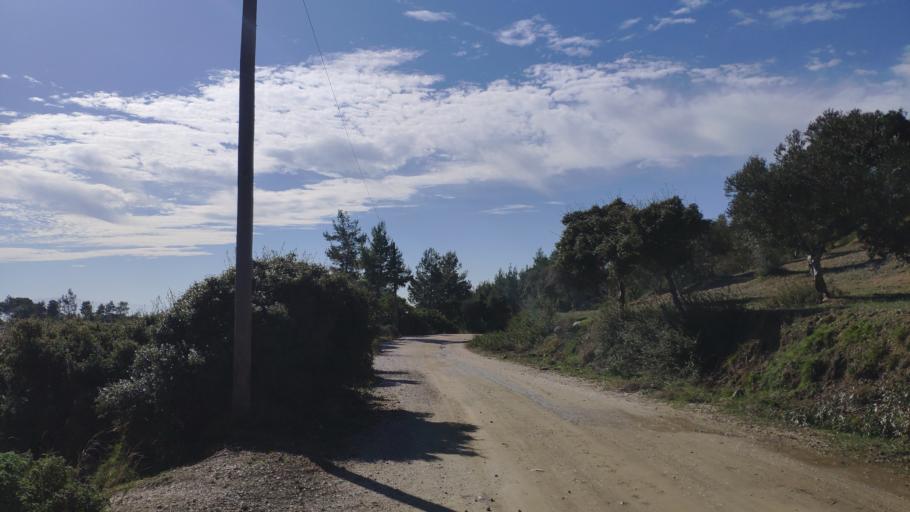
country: GR
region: Attica
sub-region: Nomarchia Anatolikis Attikis
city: Varybobi
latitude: 38.1508
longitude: 23.7748
